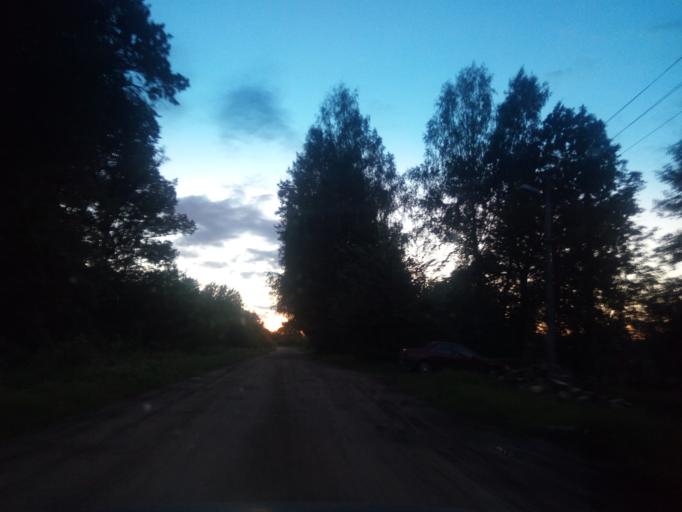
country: BY
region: Vitebsk
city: Dzisna
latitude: 55.6740
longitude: 28.3165
